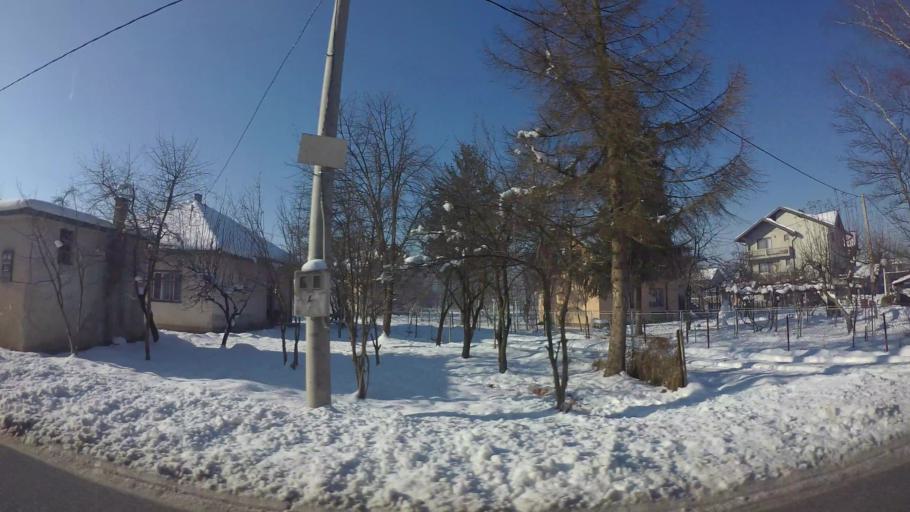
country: BA
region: Federation of Bosnia and Herzegovina
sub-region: Kanton Sarajevo
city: Sarajevo
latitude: 43.8201
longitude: 18.3813
